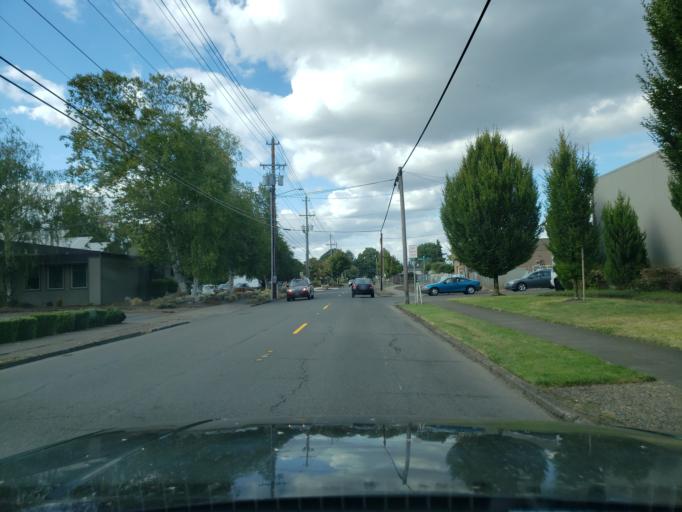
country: US
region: Oregon
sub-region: Marion County
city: Salem
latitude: 44.9603
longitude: -123.0341
